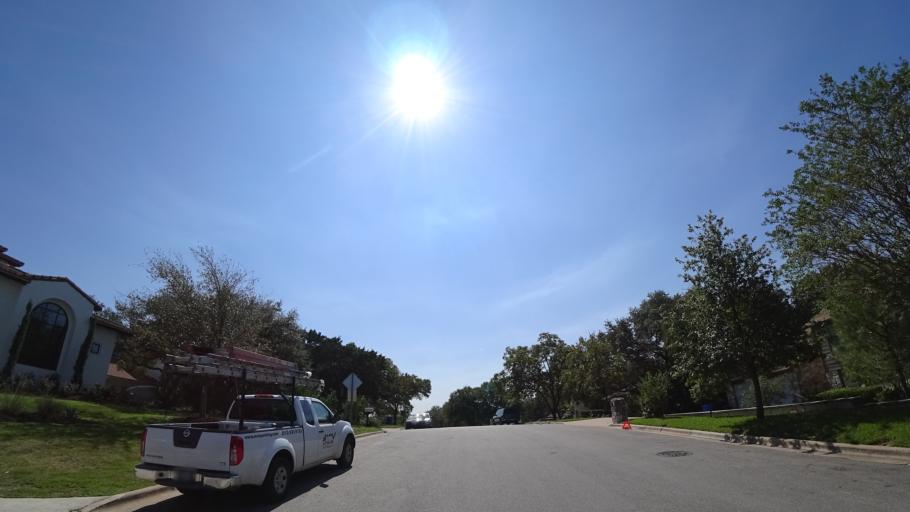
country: US
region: Texas
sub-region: Travis County
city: Rollingwood
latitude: 30.2718
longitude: -97.7849
